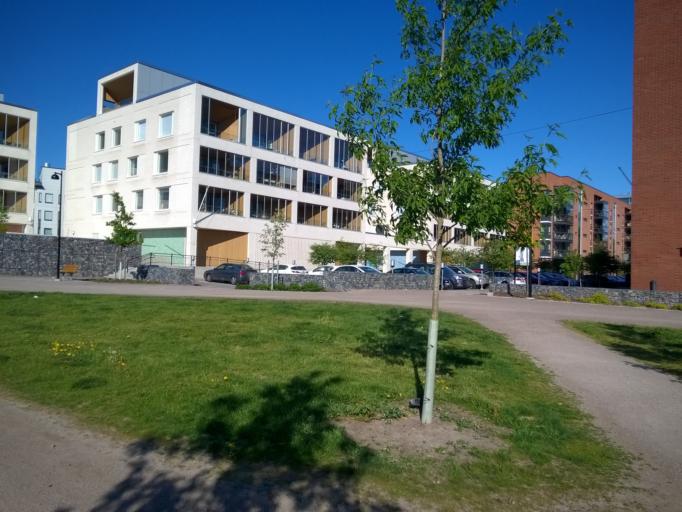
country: FI
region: Uusimaa
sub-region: Helsinki
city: Helsinki
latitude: 60.2029
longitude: 24.9754
